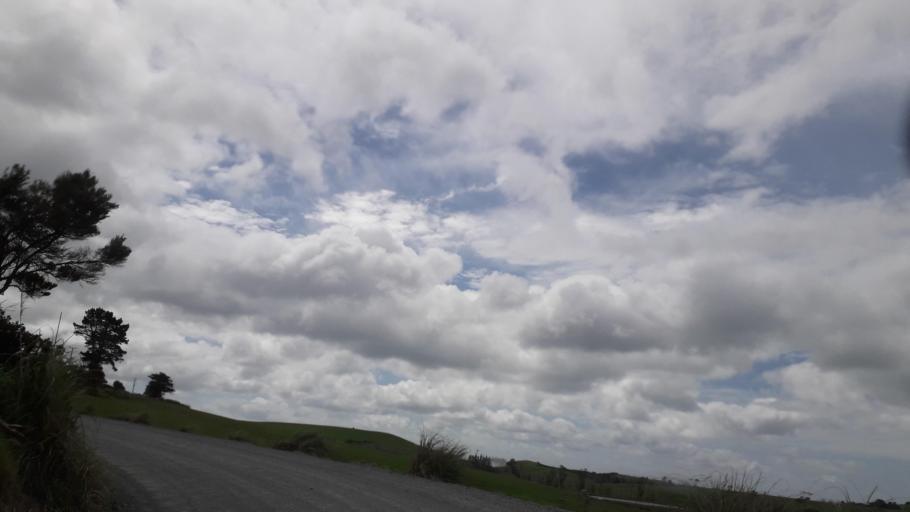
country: NZ
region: Northland
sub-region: Far North District
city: Taipa
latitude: -35.0049
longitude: 173.4319
